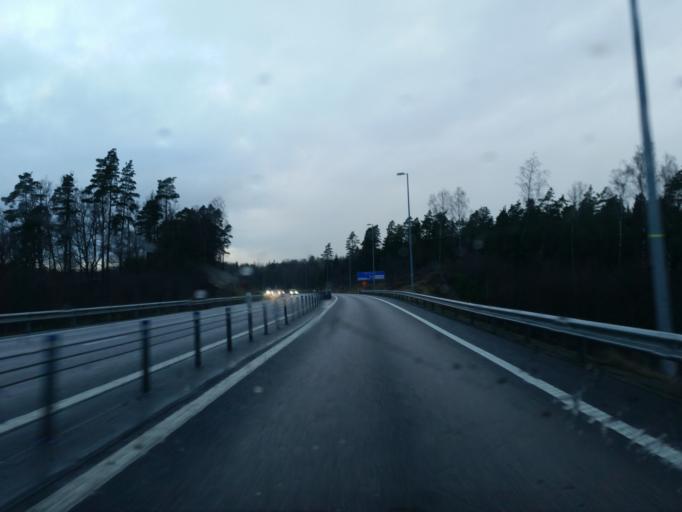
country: SE
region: Vaestra Goetaland
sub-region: Boras Kommun
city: Ganghester
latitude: 57.6786
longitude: 12.9716
